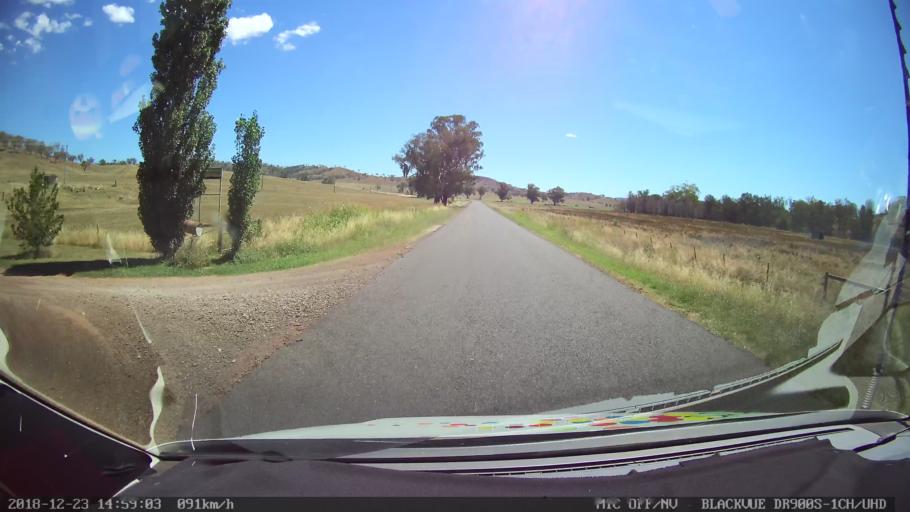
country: AU
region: New South Wales
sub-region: Tamworth Municipality
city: Manilla
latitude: -30.7212
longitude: 150.8062
